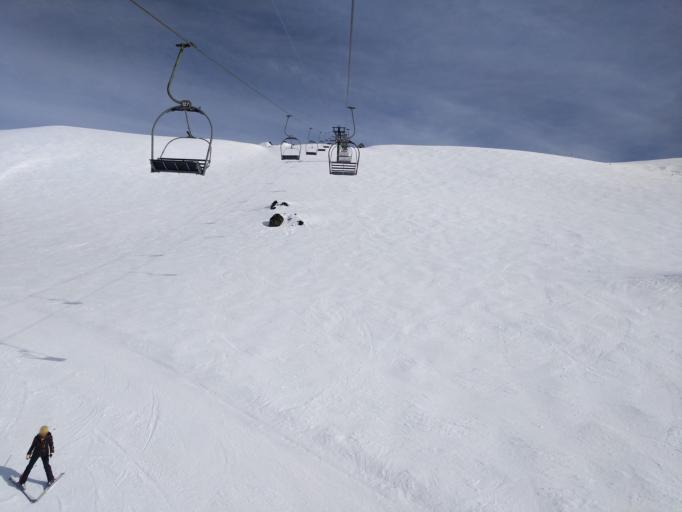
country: AR
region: Rio Negro
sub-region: Departamento de Bariloche
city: San Carlos de Bariloche
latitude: -41.1588
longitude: -71.4736
